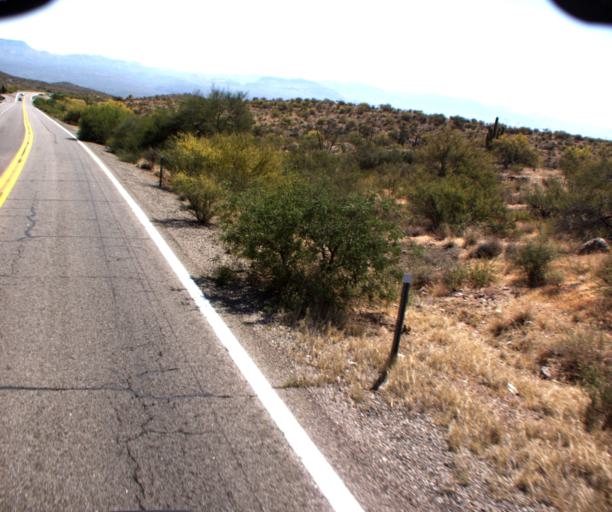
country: US
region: Arizona
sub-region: Pinal County
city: Mammoth
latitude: 32.6612
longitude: -110.6877
